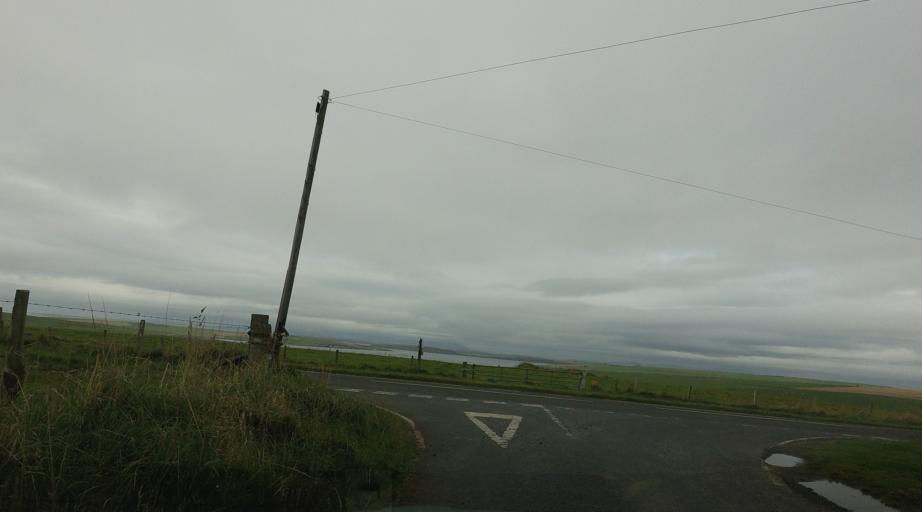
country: GB
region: Scotland
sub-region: Orkney Islands
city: Orkney
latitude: 58.8029
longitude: -2.9588
